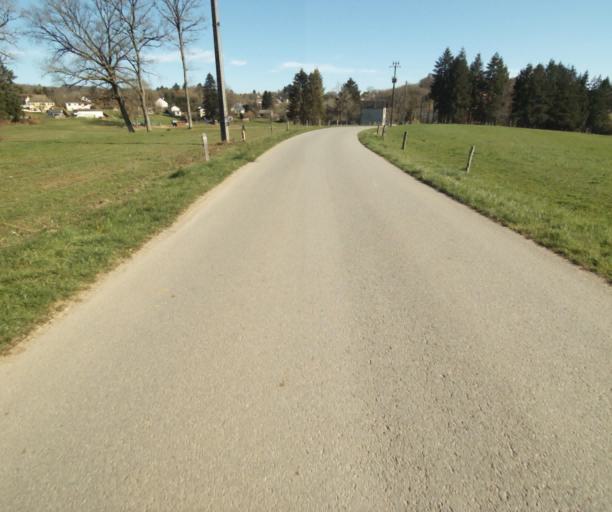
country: FR
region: Limousin
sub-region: Departement de la Correze
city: Chamboulive
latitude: 45.4723
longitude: 1.7206
